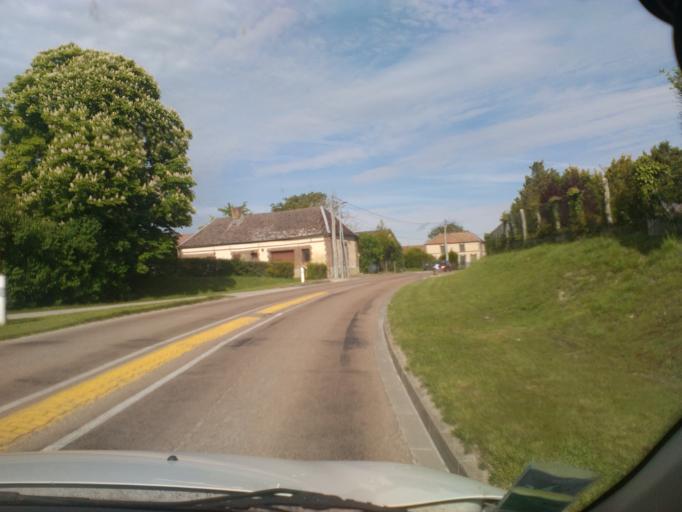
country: FR
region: Champagne-Ardenne
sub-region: Departement de l'Aube
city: Payns
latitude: 48.3678
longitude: 3.9056
